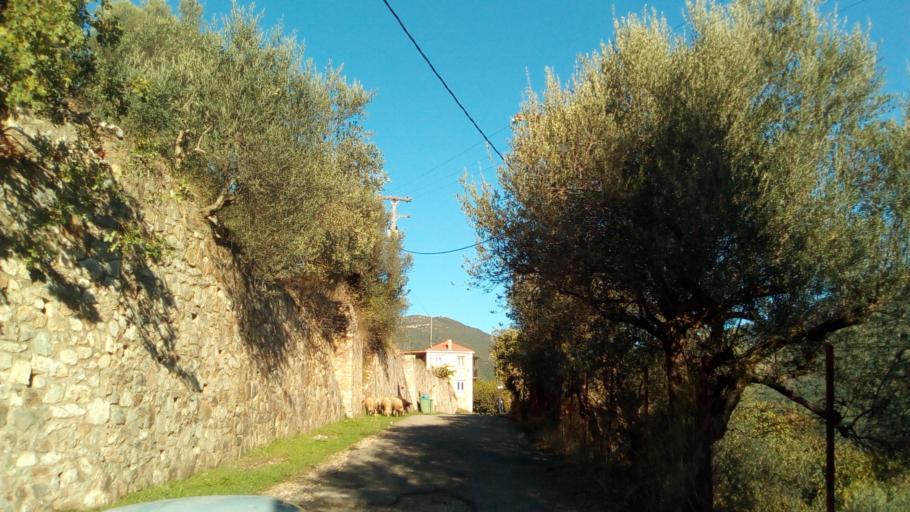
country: GR
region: West Greece
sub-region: Nomos Aitolias kai Akarnanias
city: Nafpaktos
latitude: 38.4699
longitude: 21.8622
